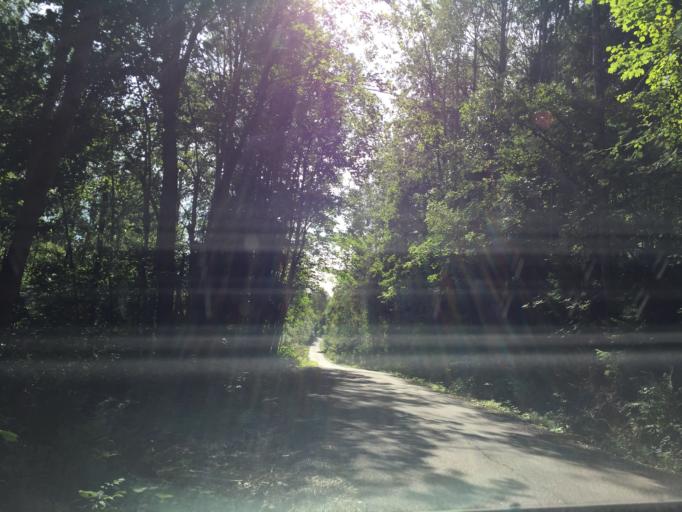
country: NO
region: Vestfold
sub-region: Hof
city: Hof
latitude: 59.4678
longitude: 10.1450
